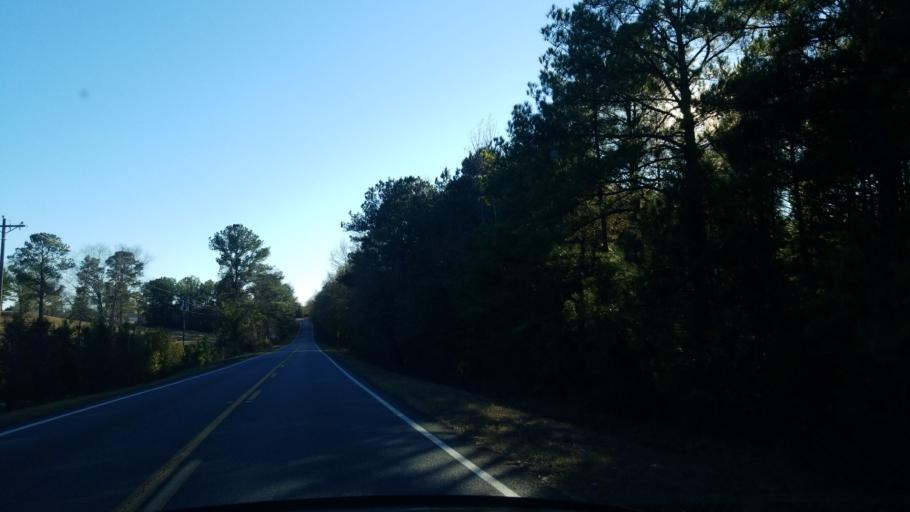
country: US
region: Georgia
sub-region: Talbot County
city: Talbotton
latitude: 32.5430
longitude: -84.6015
